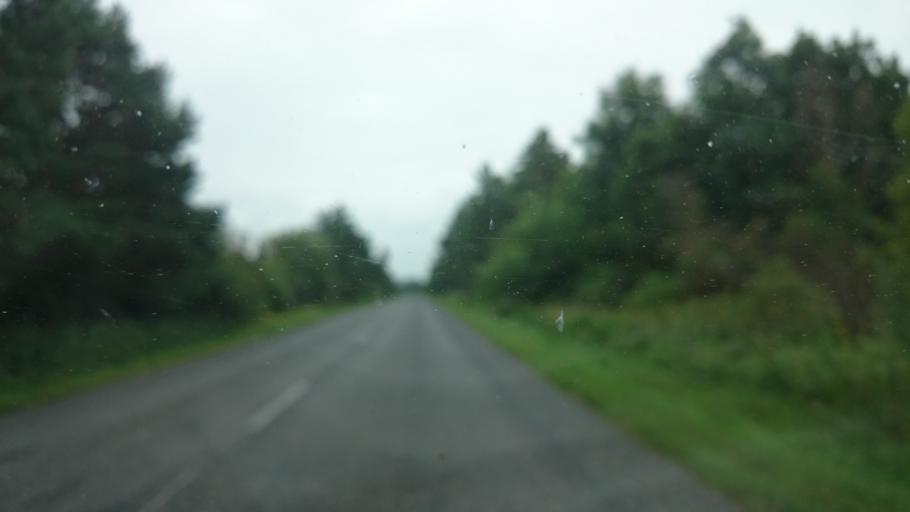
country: EE
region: Saare
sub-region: Orissaare vald
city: Orissaare
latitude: 58.5783
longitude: 23.0281
